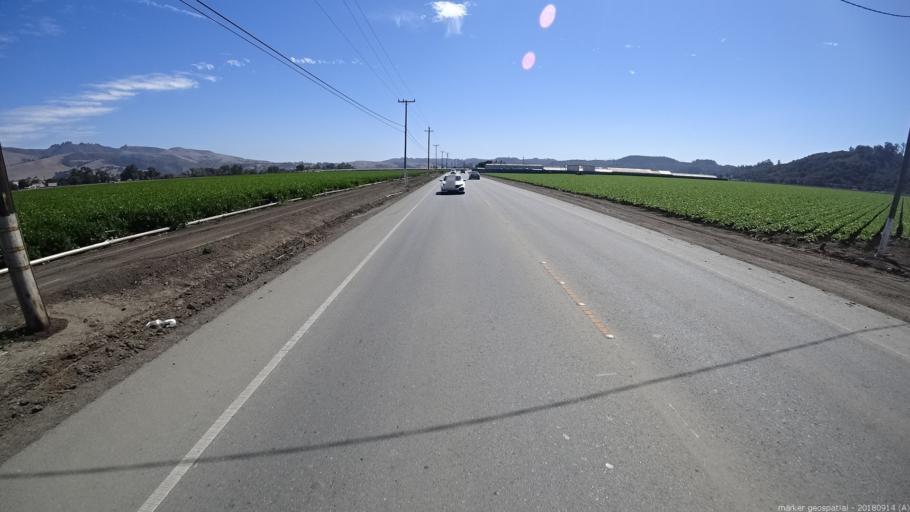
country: US
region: California
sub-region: Monterey County
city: Pajaro
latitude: 36.9028
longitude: -121.6987
